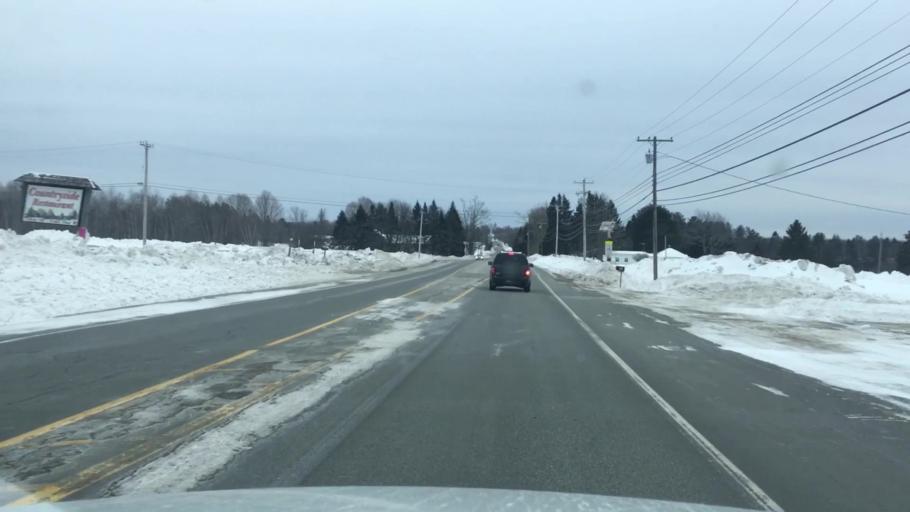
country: US
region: Maine
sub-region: Penobscot County
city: Charleston
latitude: 45.0180
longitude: -69.0283
